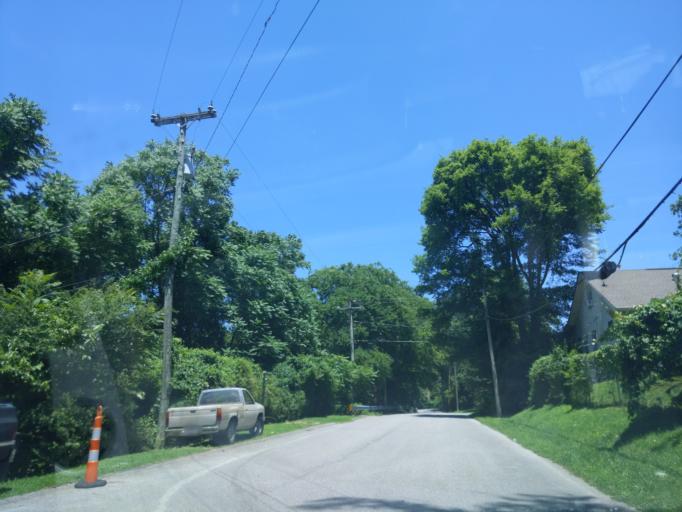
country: US
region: Tennessee
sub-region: Davidson County
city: Nashville
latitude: 36.1690
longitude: -86.7451
